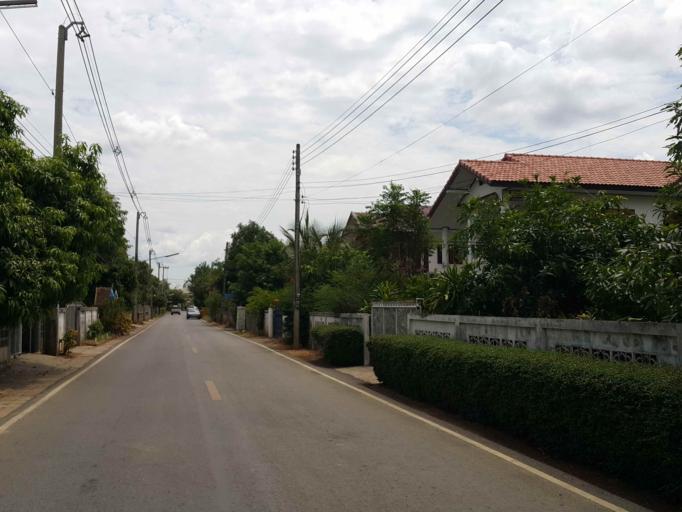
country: TH
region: Sukhothai
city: Thung Saliam
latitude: 17.3208
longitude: 99.5486
